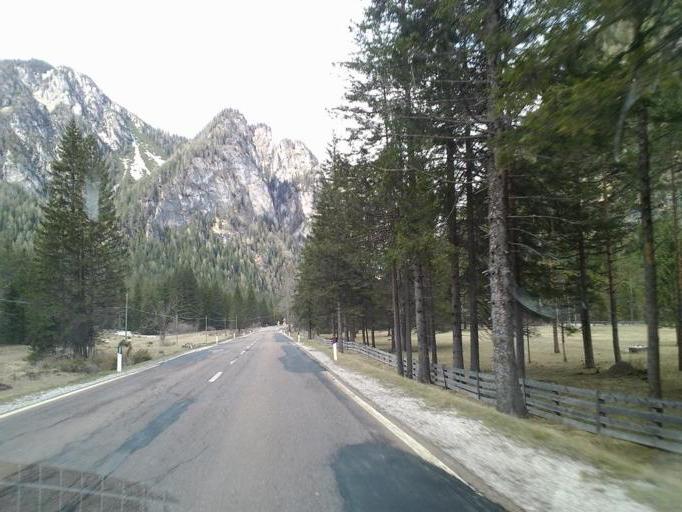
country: IT
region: Trentino-Alto Adige
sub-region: Bolzano
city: Dobbiaco
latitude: 46.6682
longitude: 12.2217
